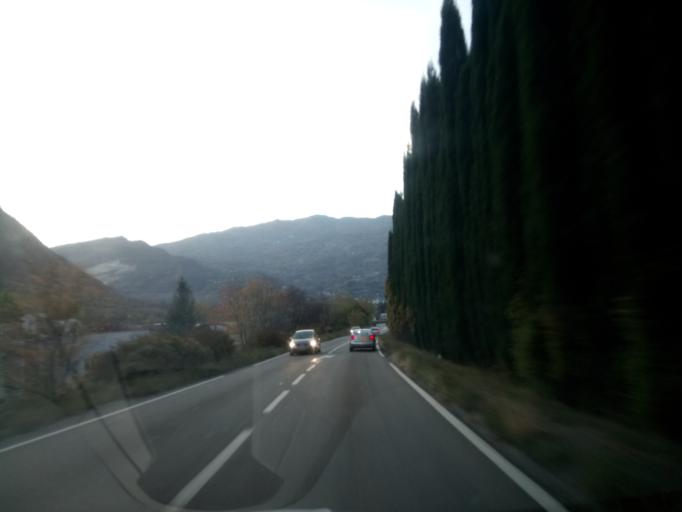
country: FR
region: Rhone-Alpes
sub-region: Departement de la Savoie
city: Villargondran
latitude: 45.2670
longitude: 6.3732
